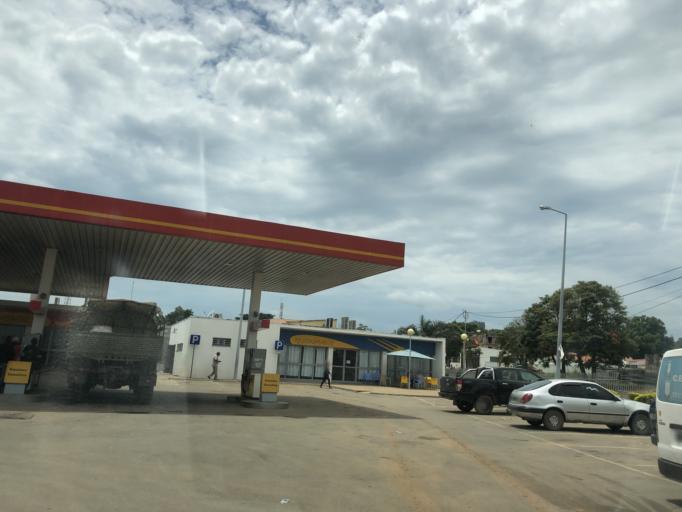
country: AO
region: Cuanza Sul
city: Quibala
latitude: -10.7317
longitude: 14.9796
